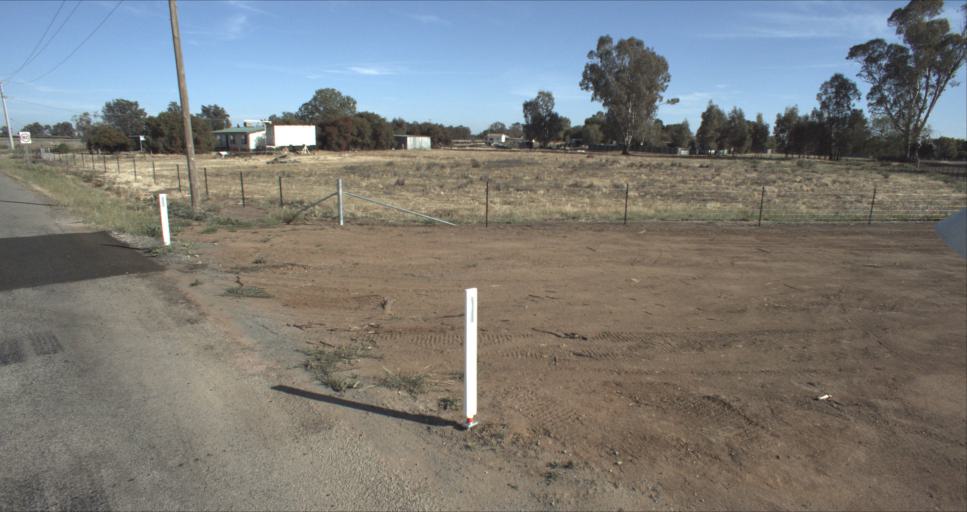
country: AU
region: New South Wales
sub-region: Leeton
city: Leeton
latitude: -34.5960
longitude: 146.4067
